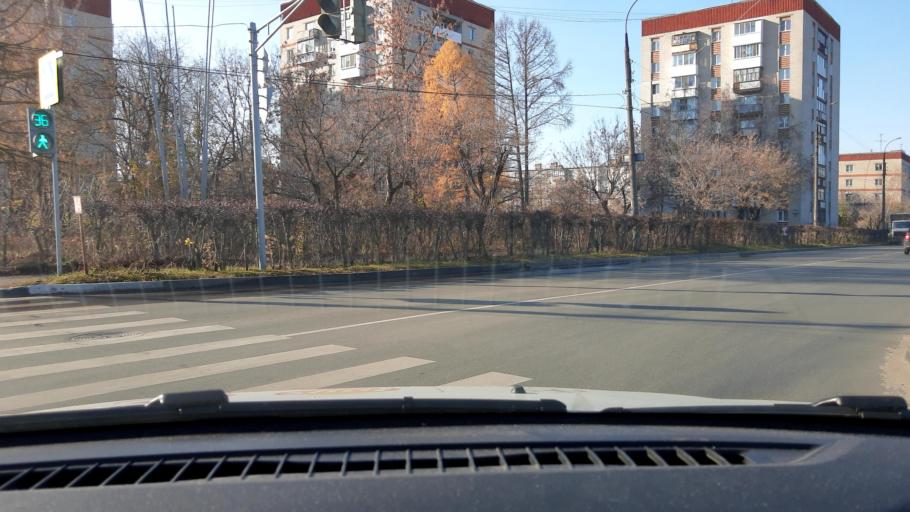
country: RU
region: Nizjnij Novgorod
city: Dzerzhinsk
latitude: 56.2555
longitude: 43.4667
